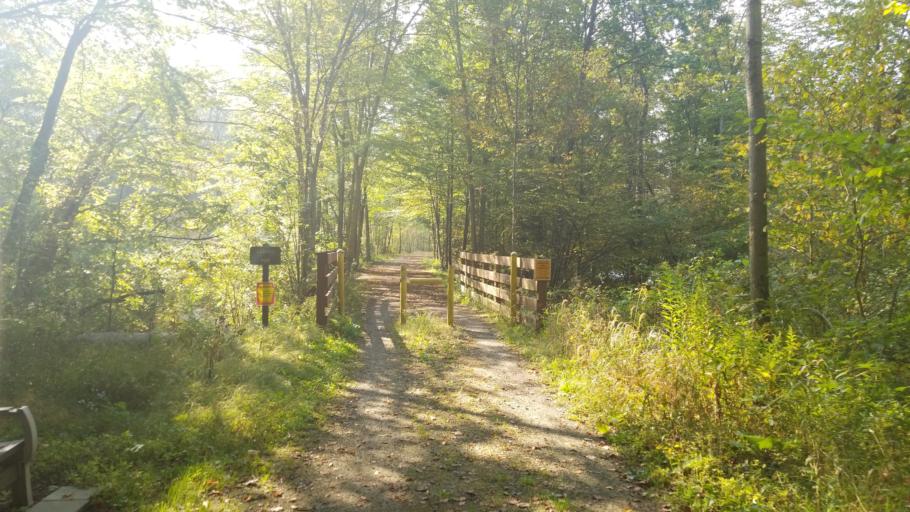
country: US
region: Pennsylvania
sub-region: Jefferson County
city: Brockway
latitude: 41.3560
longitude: -78.8184
